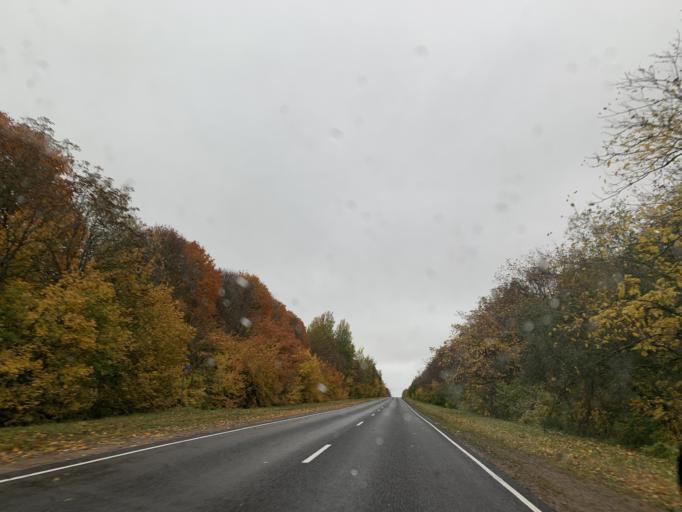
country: BY
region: Minsk
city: Haradzyeya
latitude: 53.3870
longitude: 26.5682
